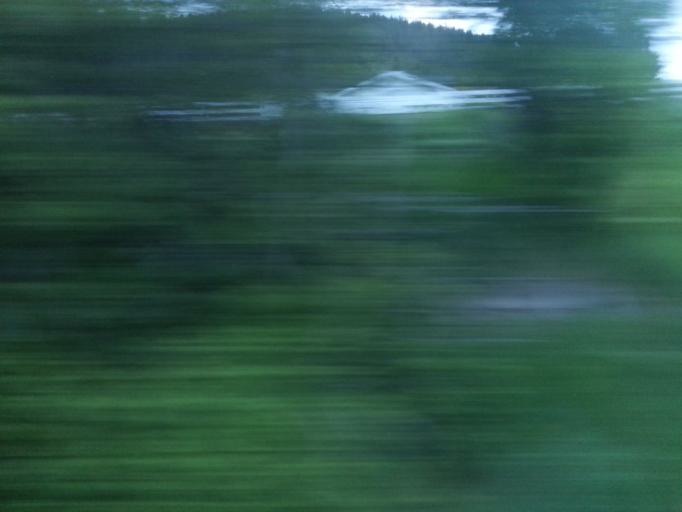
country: NO
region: Oppland
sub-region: Dovre
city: Dombas
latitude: 62.0524
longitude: 9.1439
